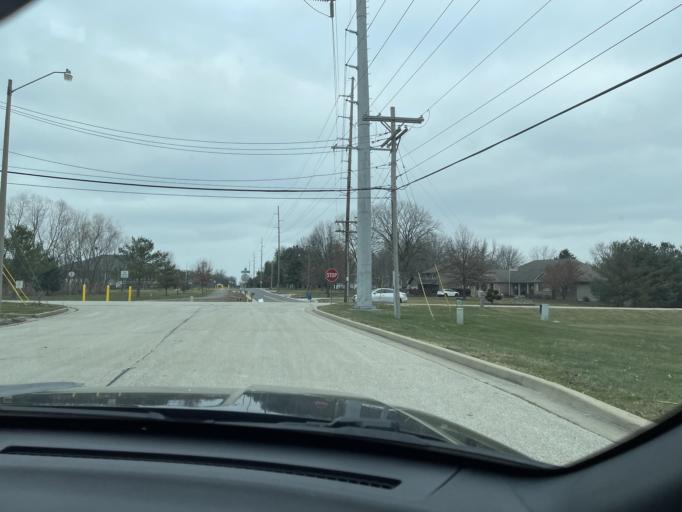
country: US
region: Illinois
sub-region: Sangamon County
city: Rochester
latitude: 39.7542
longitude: -89.5787
